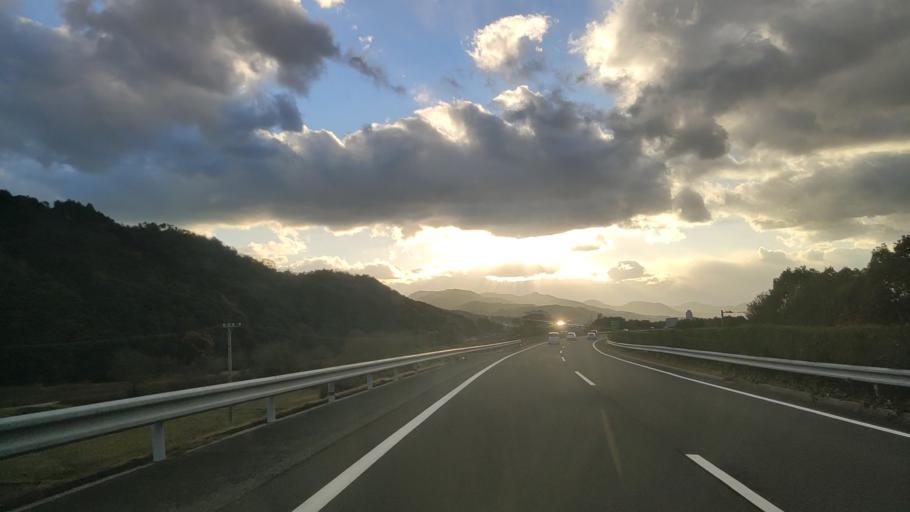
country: JP
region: Ehime
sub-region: Shikoku-chuo Shi
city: Matsuyama
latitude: 33.7899
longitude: 132.8949
